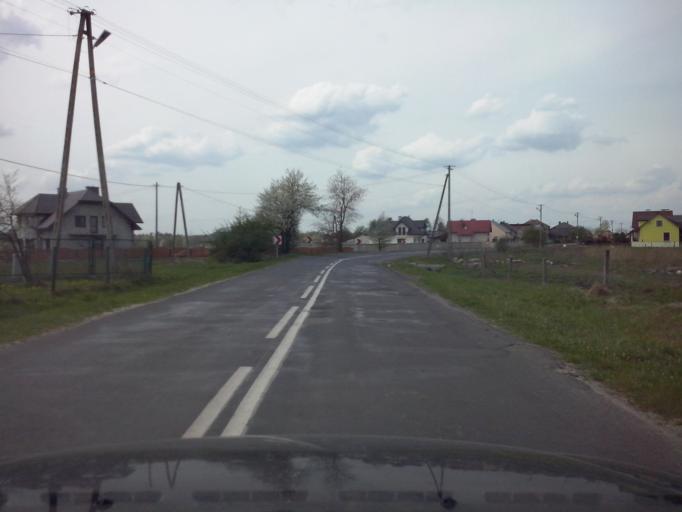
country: PL
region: Subcarpathian Voivodeship
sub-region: Powiat lezajski
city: Letownia
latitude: 50.3656
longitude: 22.2242
